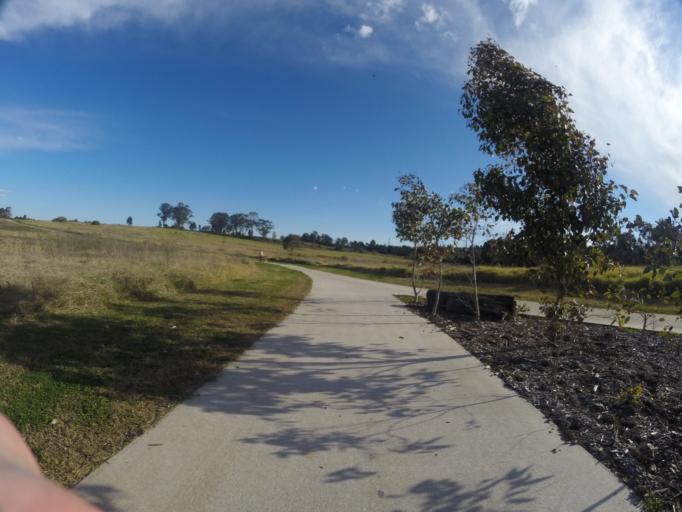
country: AU
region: New South Wales
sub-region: Fairfield
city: Horsley Park
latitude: -33.8541
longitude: 150.8726
